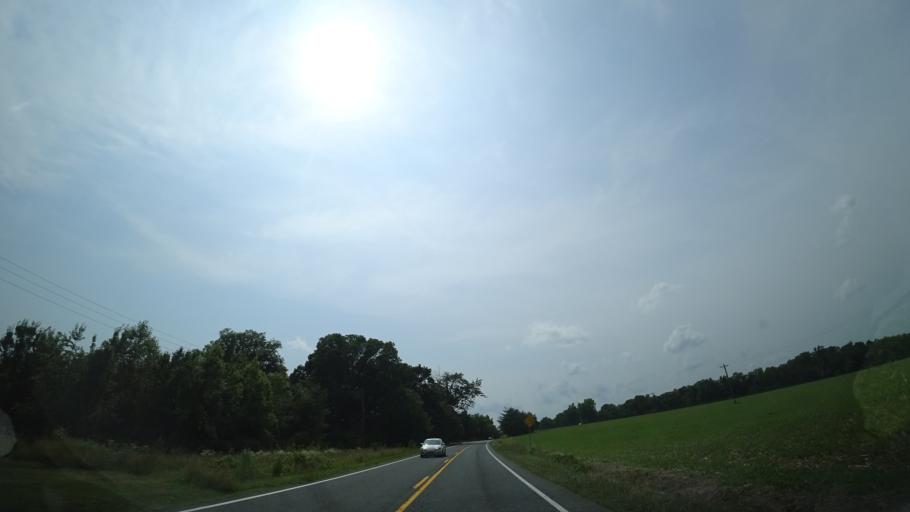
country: US
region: Virginia
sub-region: Spotsylvania County
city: Spotsylvania Courthouse
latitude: 38.1342
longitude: -77.5271
